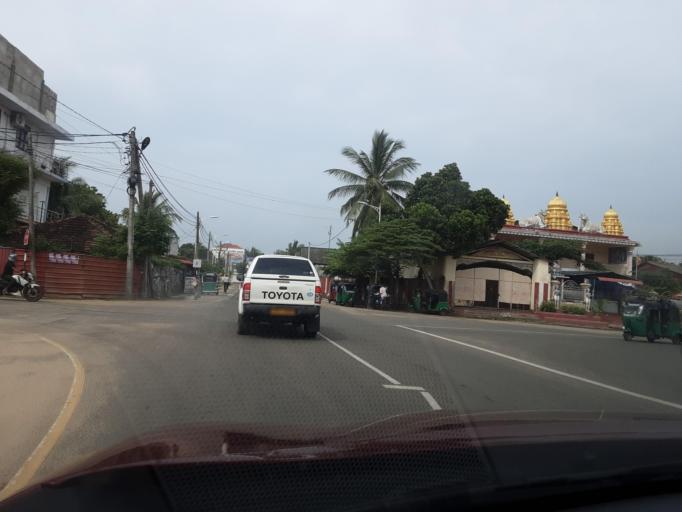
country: LK
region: Northern Province
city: Jaffna
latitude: 9.6737
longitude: 80.0290
